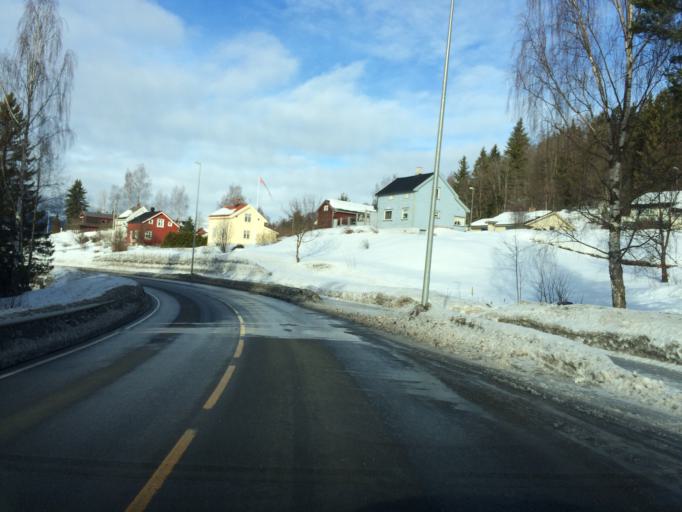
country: NO
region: Oppland
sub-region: Gausdal
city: Segalstad bru
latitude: 61.2248
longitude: 10.2318
